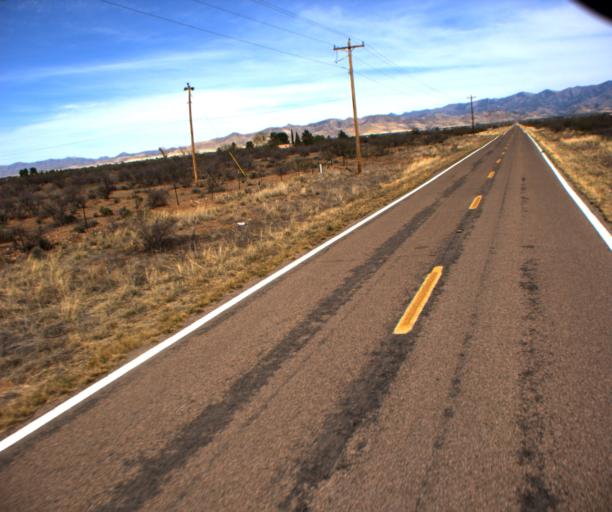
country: US
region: Arizona
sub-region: Cochise County
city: Willcox
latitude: 31.8760
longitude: -109.5514
